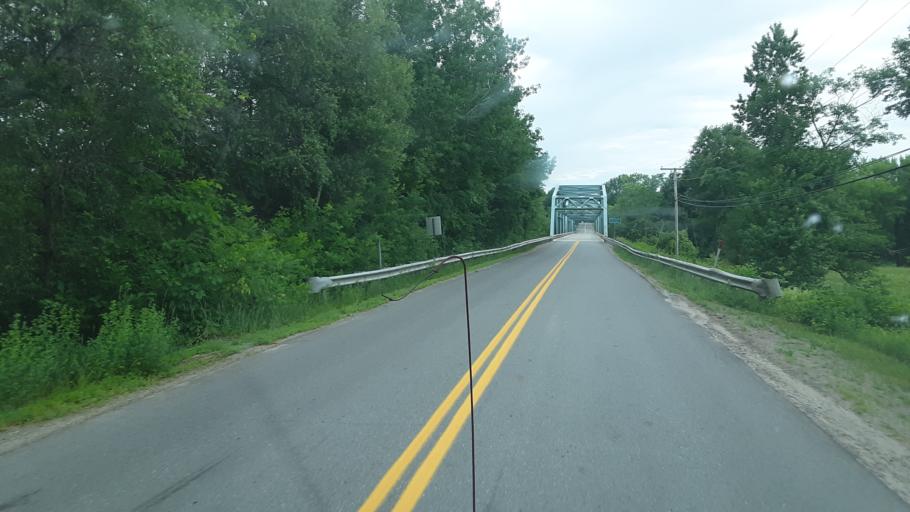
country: US
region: Maine
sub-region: Penobscot County
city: Lincoln
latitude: 45.4311
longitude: -68.4578
